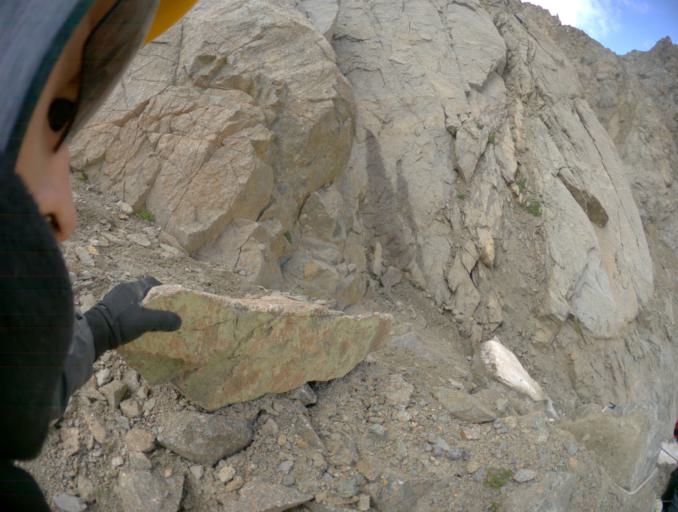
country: RU
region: Kabardino-Balkariya
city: Terskol
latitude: 43.3311
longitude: 42.5433
